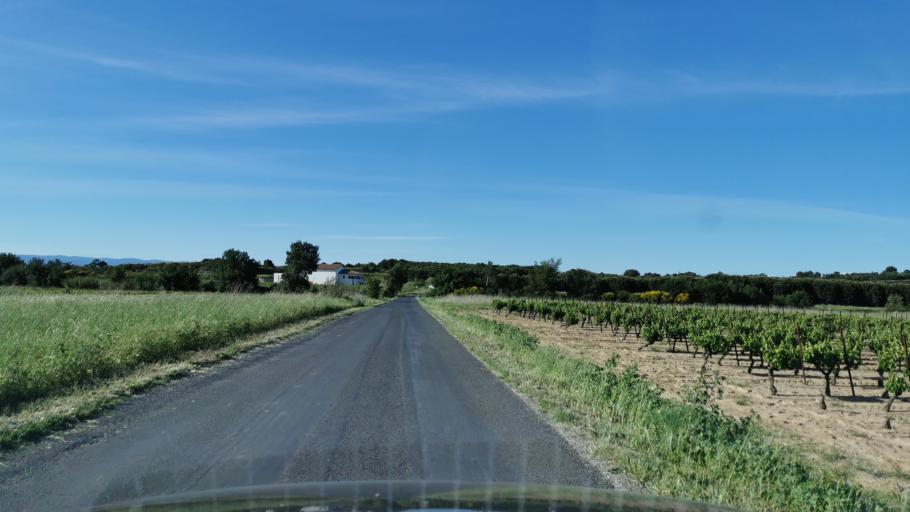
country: FR
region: Languedoc-Roussillon
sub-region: Departement de l'Aude
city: Nevian
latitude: 43.2157
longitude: 2.9126
